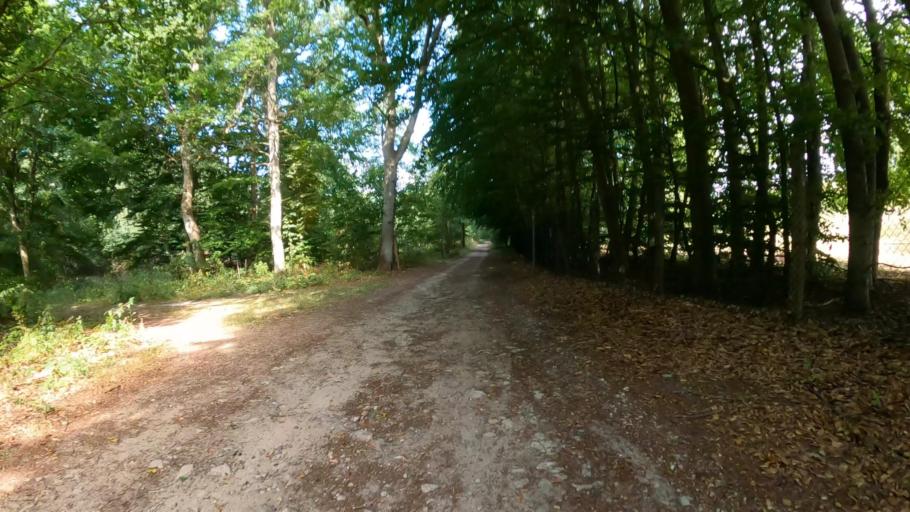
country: DE
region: Schleswig-Holstein
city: Geesthacht
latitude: 53.4236
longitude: 10.3970
